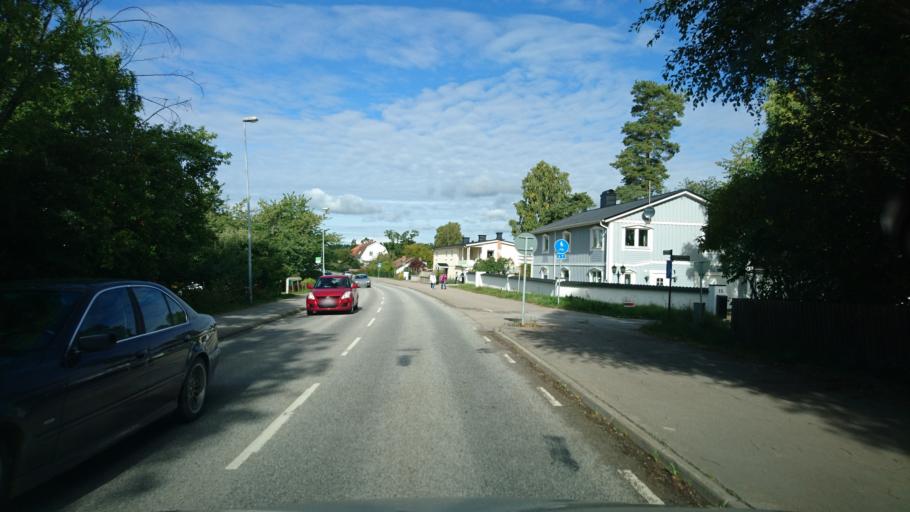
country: SE
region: Soedermanland
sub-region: Strangnas Kommun
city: Stallarholmen
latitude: 59.3602
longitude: 17.2063
